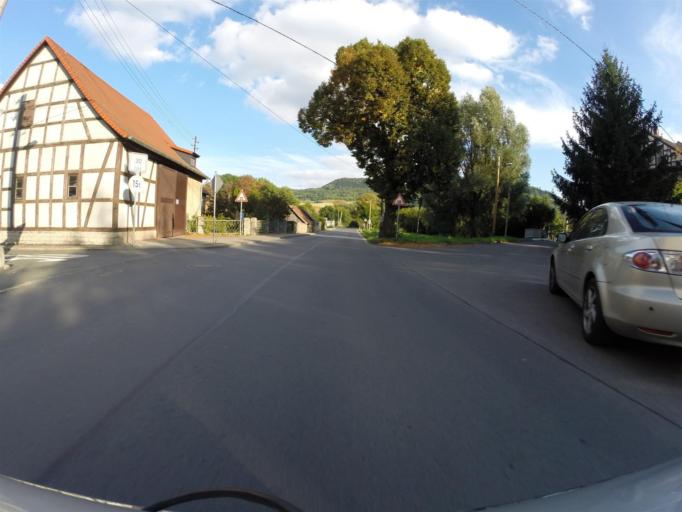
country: DE
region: Thuringia
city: Jena
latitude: 50.9510
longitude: 11.6143
